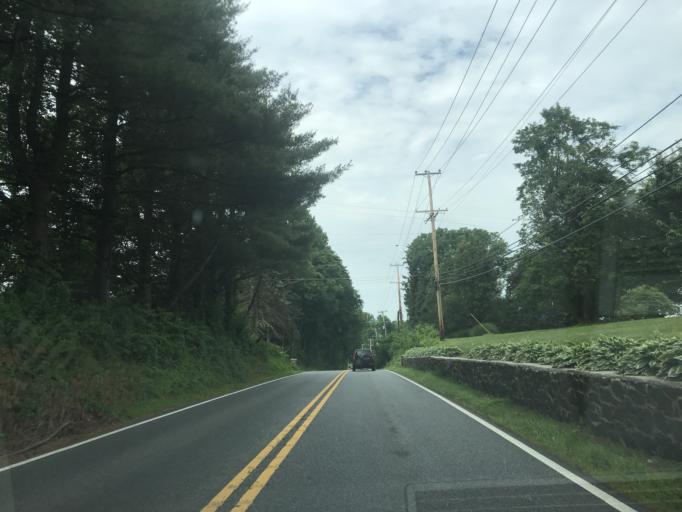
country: US
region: Maryland
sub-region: Harford County
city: Jarrettsville
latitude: 39.5487
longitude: -76.4705
